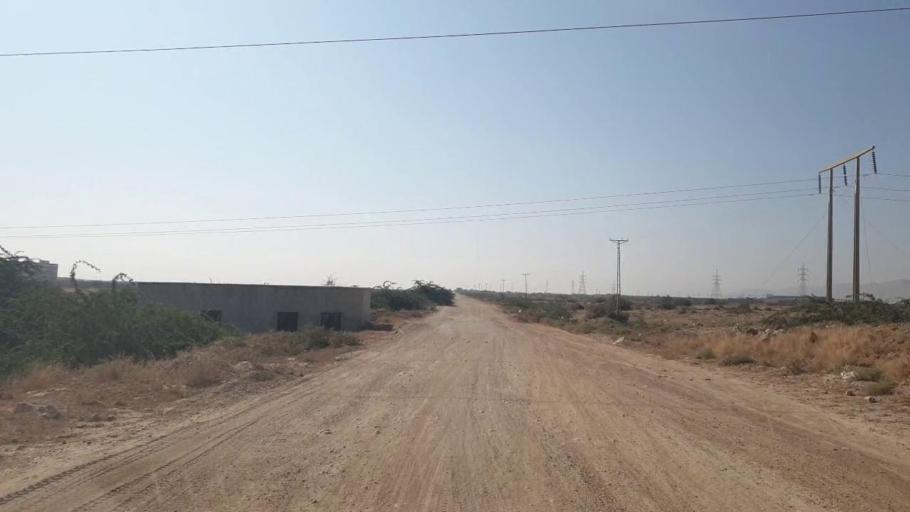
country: PK
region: Sindh
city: Gharo
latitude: 25.1638
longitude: 67.7283
